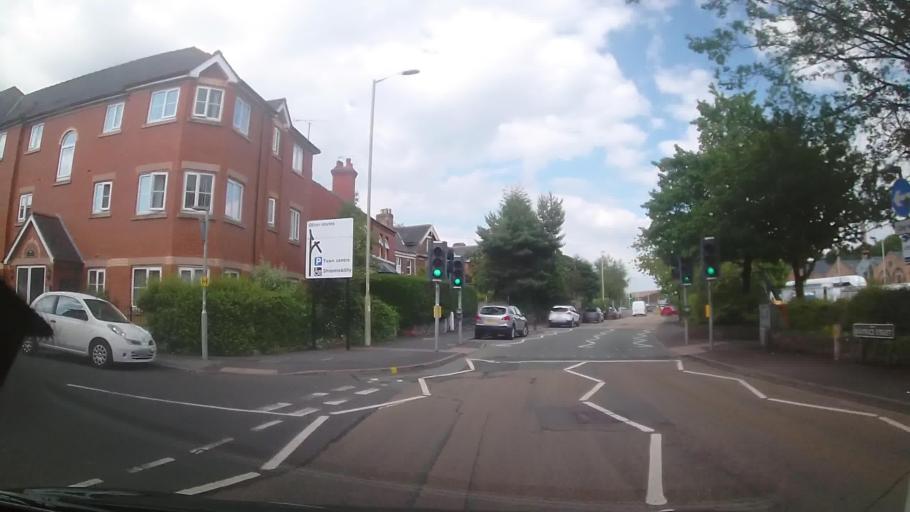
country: GB
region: England
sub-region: Shropshire
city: Oswestry
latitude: 52.8628
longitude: -3.0504
